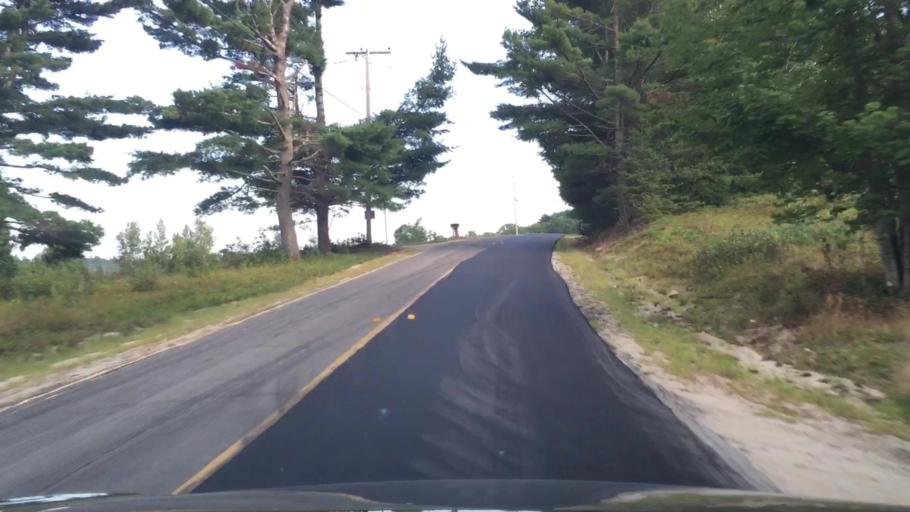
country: US
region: Maine
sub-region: Hancock County
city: Surry
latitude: 44.5159
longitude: -68.6041
